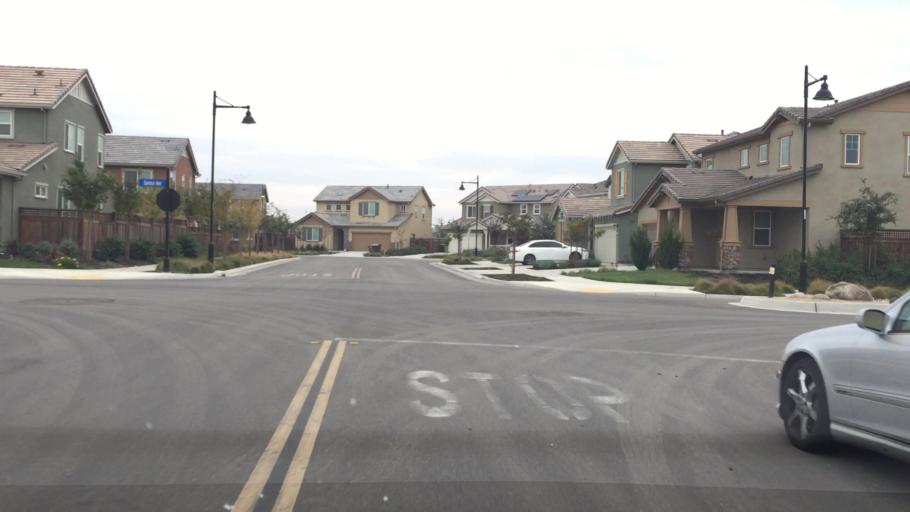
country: US
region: California
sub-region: San Joaquin County
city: Lathrop
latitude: 37.7946
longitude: -121.3208
